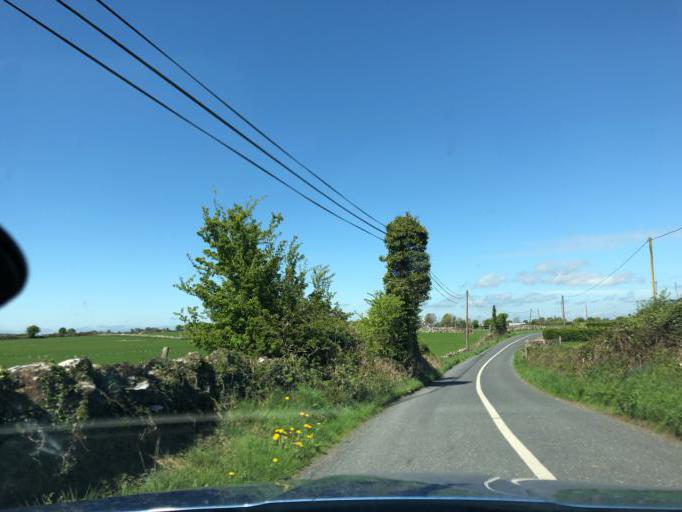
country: IE
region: Connaught
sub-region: County Galway
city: Loughrea
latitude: 53.1646
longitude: -8.4081
